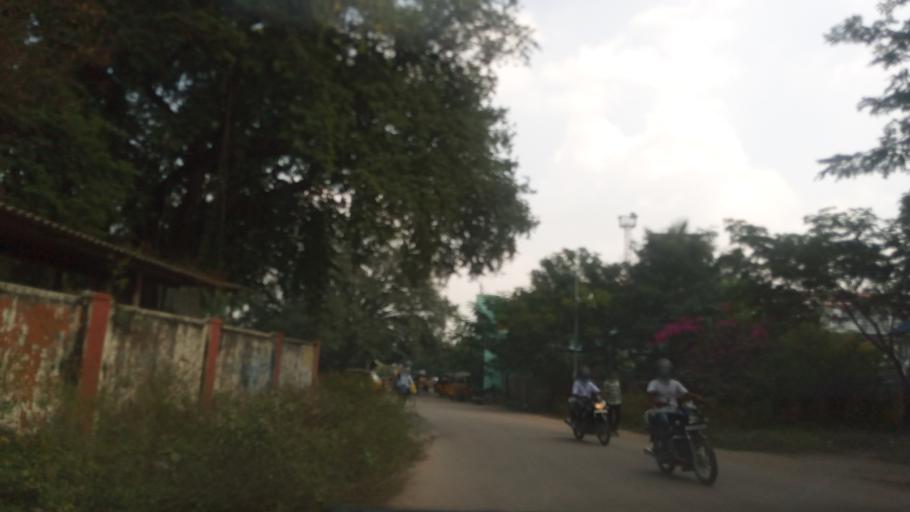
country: IN
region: Tamil Nadu
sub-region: Vellore
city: Arakkonam
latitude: 13.0823
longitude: 79.6678
